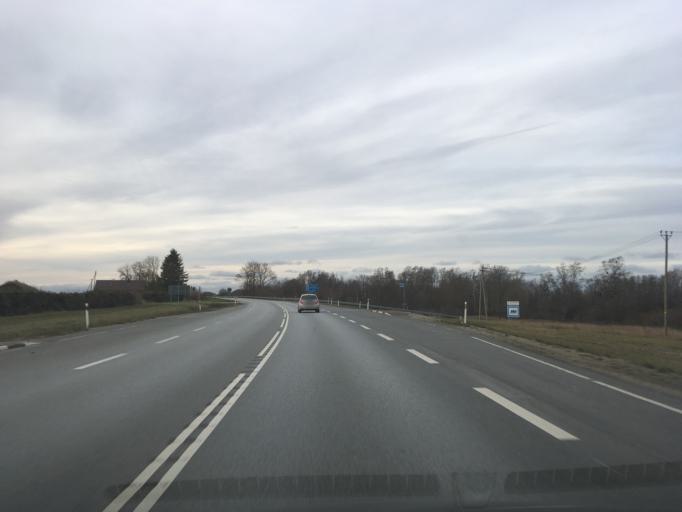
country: EE
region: Ida-Virumaa
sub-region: Kivioli linn
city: Kivioli
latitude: 59.4279
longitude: 26.9558
